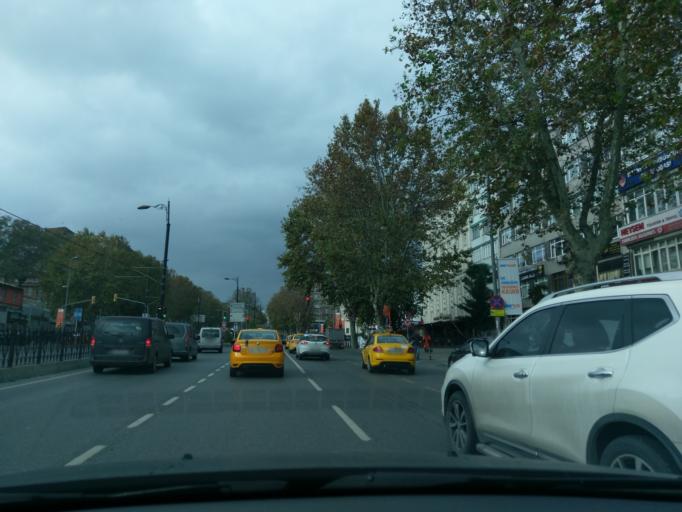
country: TR
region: Istanbul
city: Istanbul
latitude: 41.0104
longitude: 28.9461
